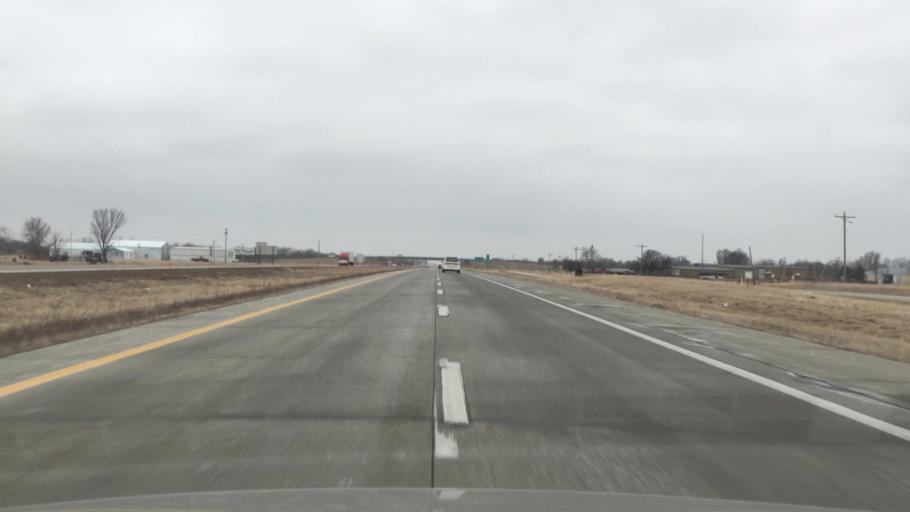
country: US
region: Missouri
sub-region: Cass County
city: Harrisonville
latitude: 38.6093
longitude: -94.3489
